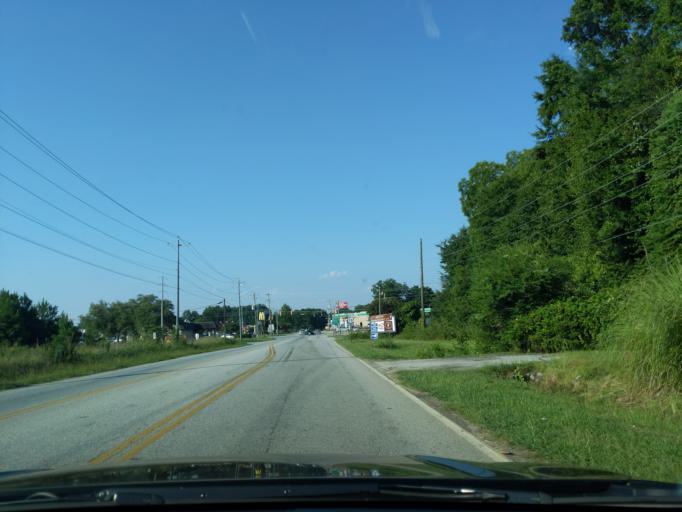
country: US
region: South Carolina
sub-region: Newberry County
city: Newberry
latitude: 34.2860
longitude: -81.5970
